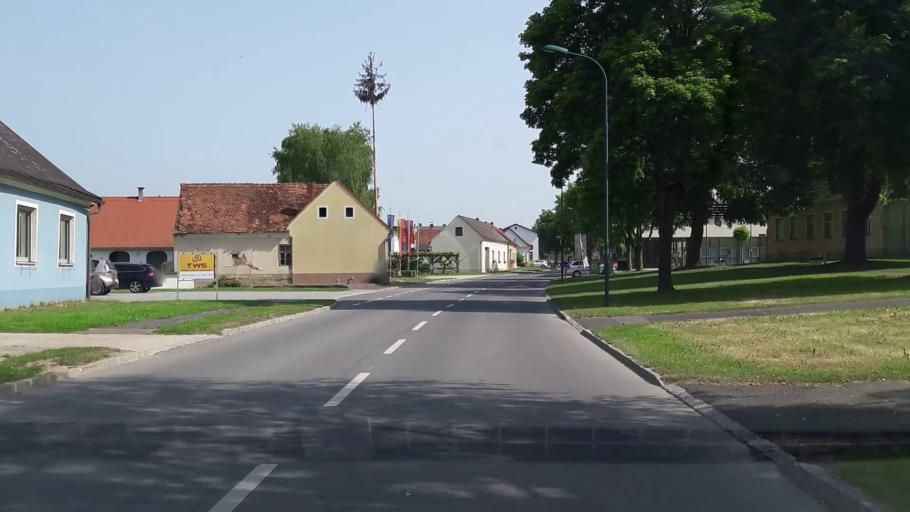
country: AT
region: Burgenland
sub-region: Politischer Bezirk Jennersdorf
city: Deutsch Kaltenbrunn
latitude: 47.0867
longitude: 16.1062
